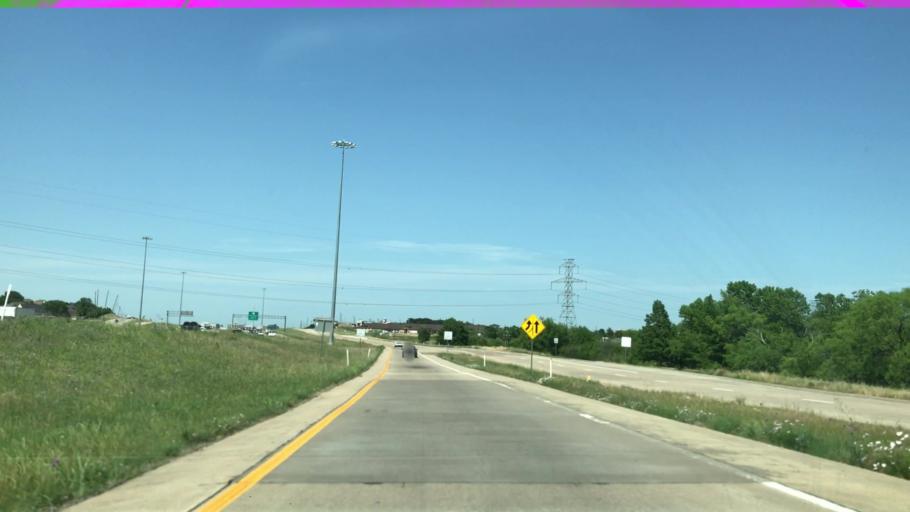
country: US
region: Texas
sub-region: Dallas County
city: Irving
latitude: 32.8680
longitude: -96.9995
